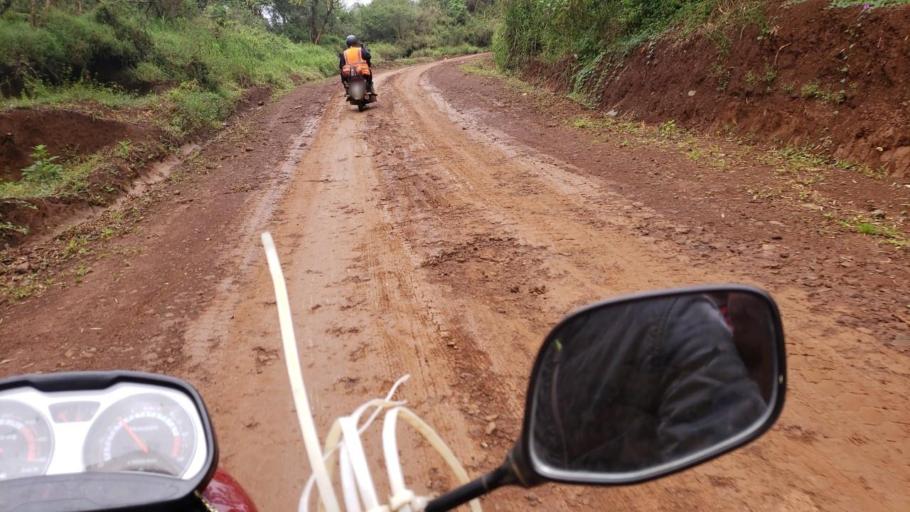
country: CD
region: South Kivu
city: Kabare
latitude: -2.2659
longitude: 28.6602
